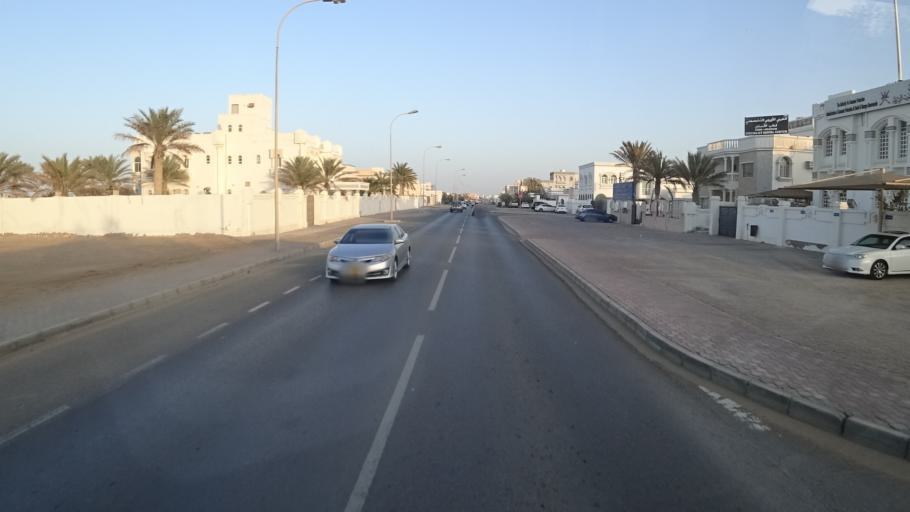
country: OM
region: Ash Sharqiyah
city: Sur
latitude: 22.5934
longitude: 59.4971
